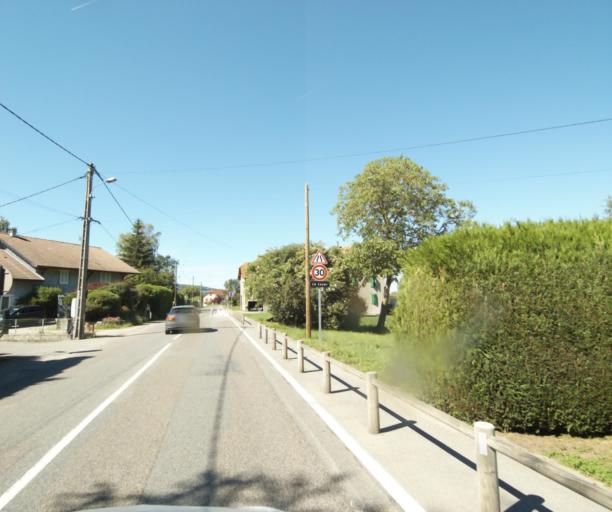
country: FR
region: Rhone-Alpes
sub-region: Departement de la Haute-Savoie
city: Bons-en-Chablais
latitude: 46.2733
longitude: 6.3612
